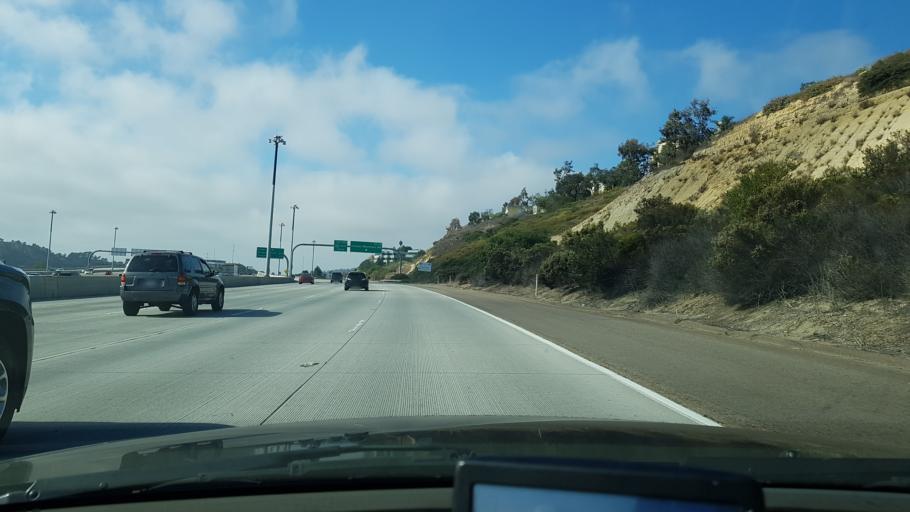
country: US
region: California
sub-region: San Diego County
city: Del Mar
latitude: 32.9149
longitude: -117.2300
